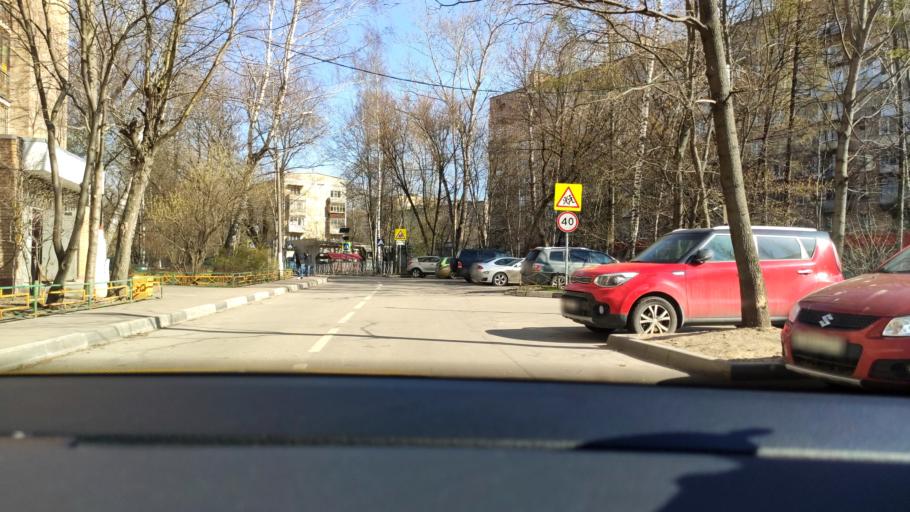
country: RU
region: Moskovskaya
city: Levoberezhnaya
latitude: 55.8904
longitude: 37.4734
